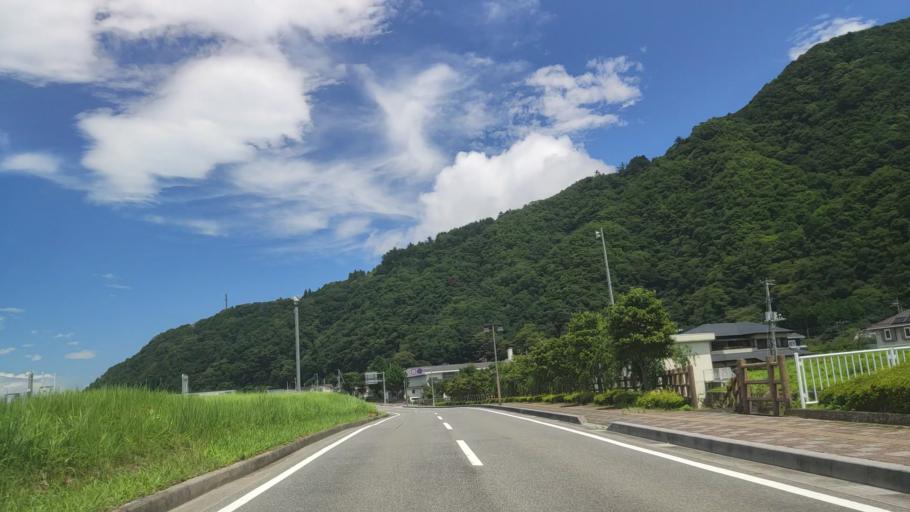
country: JP
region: Shizuoka
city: Fujinomiya
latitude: 35.3663
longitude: 138.4535
